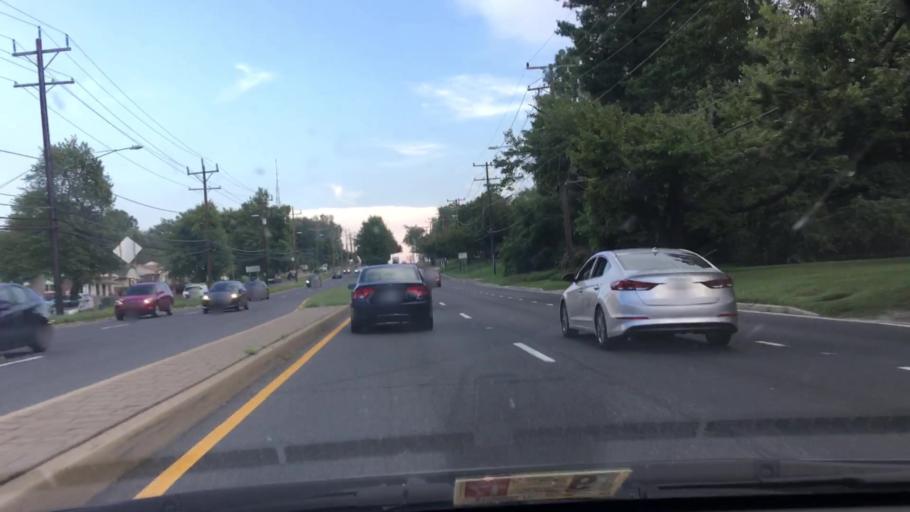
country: US
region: Maryland
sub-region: Montgomery County
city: Wheaton
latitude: 39.0438
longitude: -77.0626
